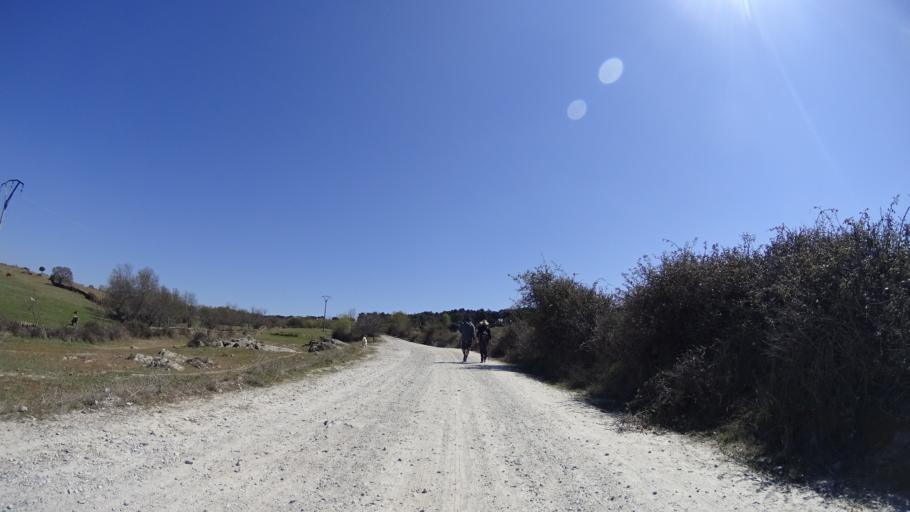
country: ES
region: Madrid
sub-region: Provincia de Madrid
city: Colmenar Viejo
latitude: 40.7042
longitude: -3.7740
